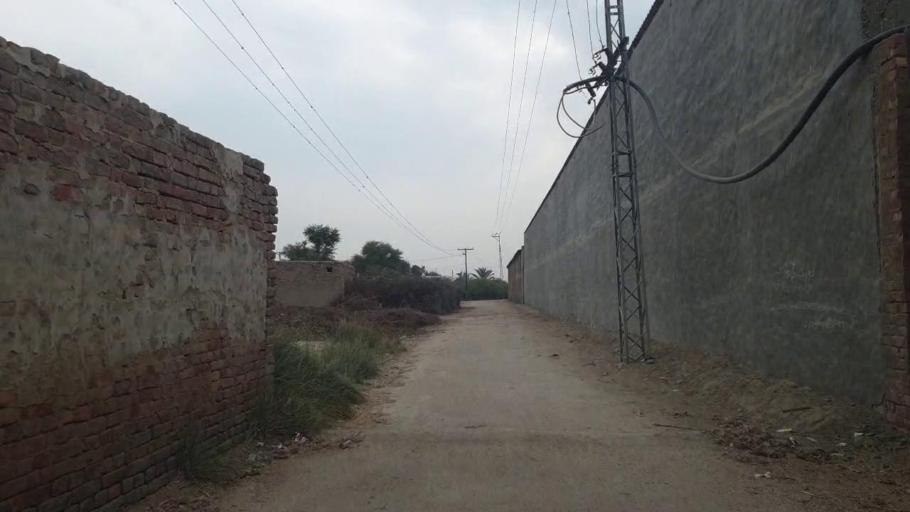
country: PK
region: Sindh
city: Shahdadpur
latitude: 25.9279
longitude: 68.6607
